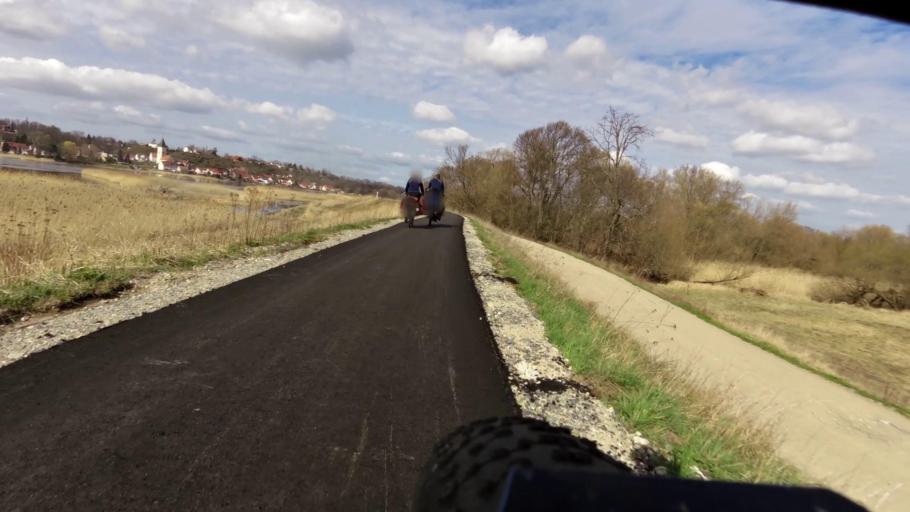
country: DE
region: Brandenburg
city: Lebus
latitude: 52.4205
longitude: 14.5477
